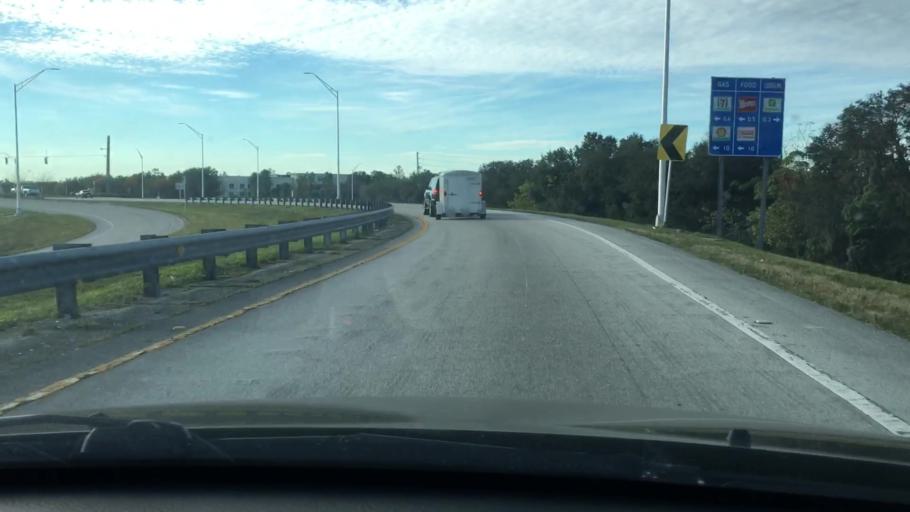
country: US
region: Florida
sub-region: Volusia County
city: Holly Hill
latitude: 29.2208
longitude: -81.1053
